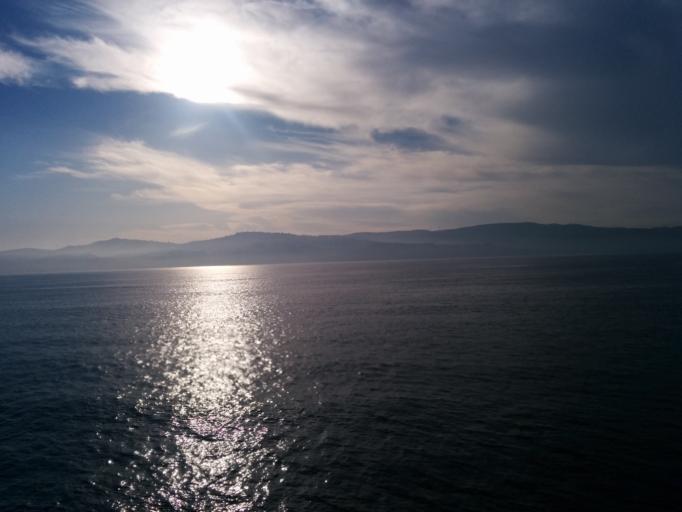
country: MA
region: Tanger-Tetouan
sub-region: Tanger-Assilah
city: Tangier
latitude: 35.8054
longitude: -5.7839
